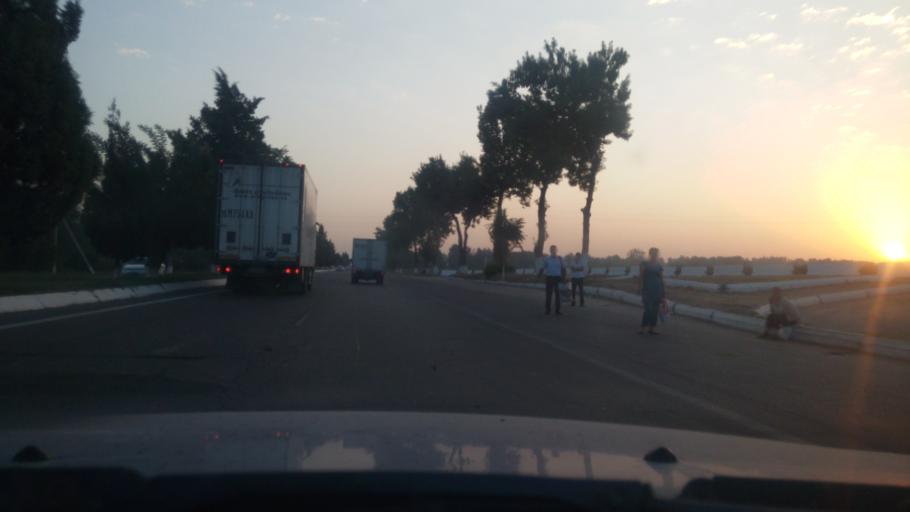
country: UZ
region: Toshkent
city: Zafar
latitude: 41.0359
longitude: 68.8747
